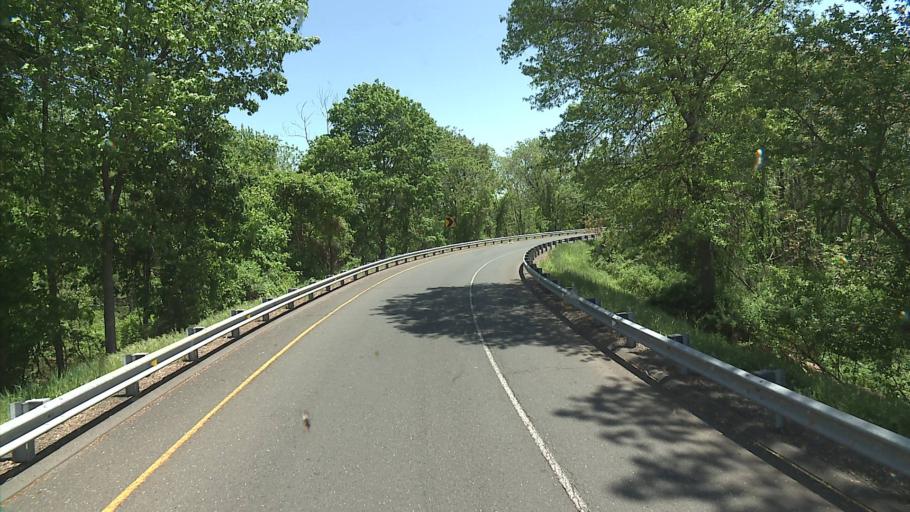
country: US
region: Connecticut
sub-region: Hartford County
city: East Hartford
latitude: 41.7654
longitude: -72.6444
